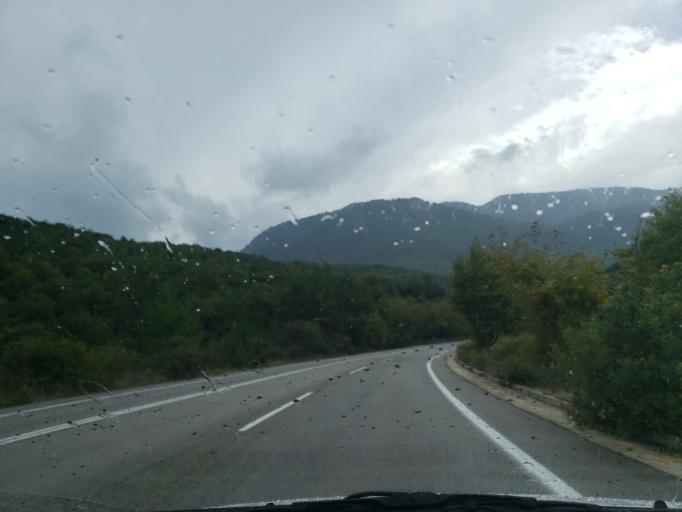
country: GR
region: Central Greece
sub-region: Nomos Fthiotidos
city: Anthili
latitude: 38.7896
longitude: 22.4942
